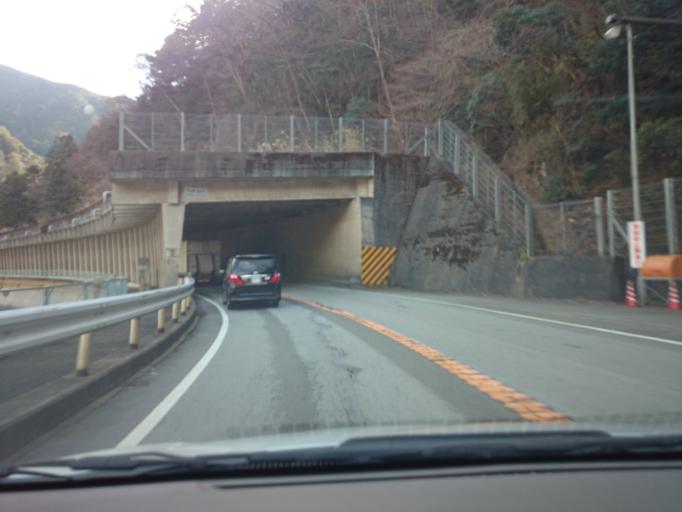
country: JP
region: Gifu
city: Gujo
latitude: 35.7575
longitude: 137.2259
